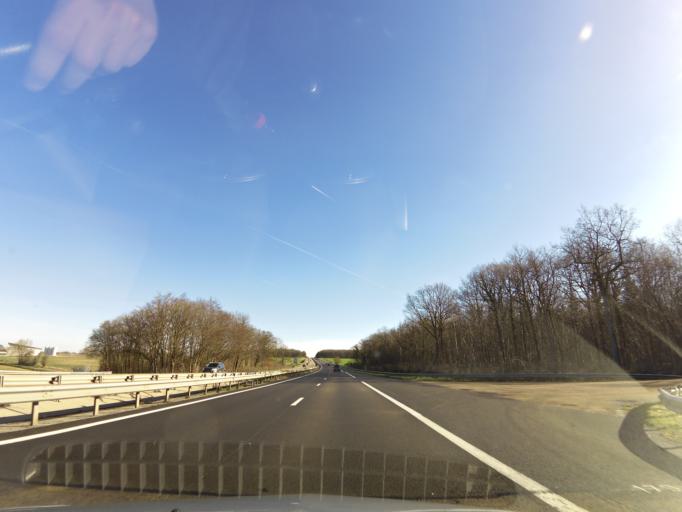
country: FR
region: Bourgogne
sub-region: Departement de l'Yonne
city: Vermenton
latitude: 47.7148
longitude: 3.7696
